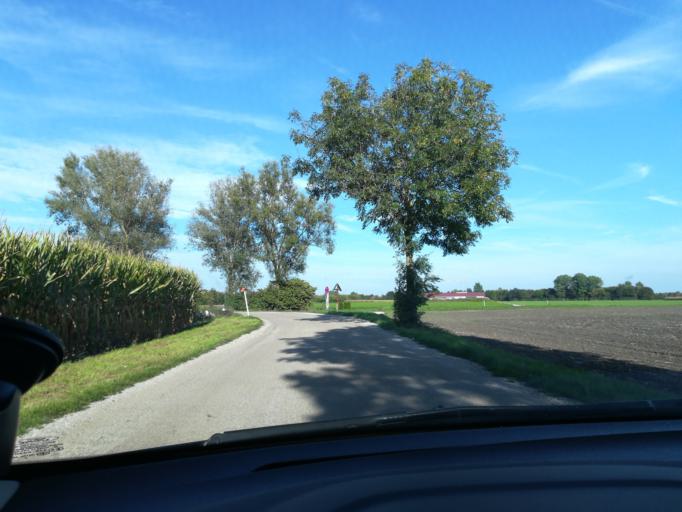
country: DE
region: Bavaria
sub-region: Upper Bavaria
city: Hallbergmoos
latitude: 48.2927
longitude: 11.7262
